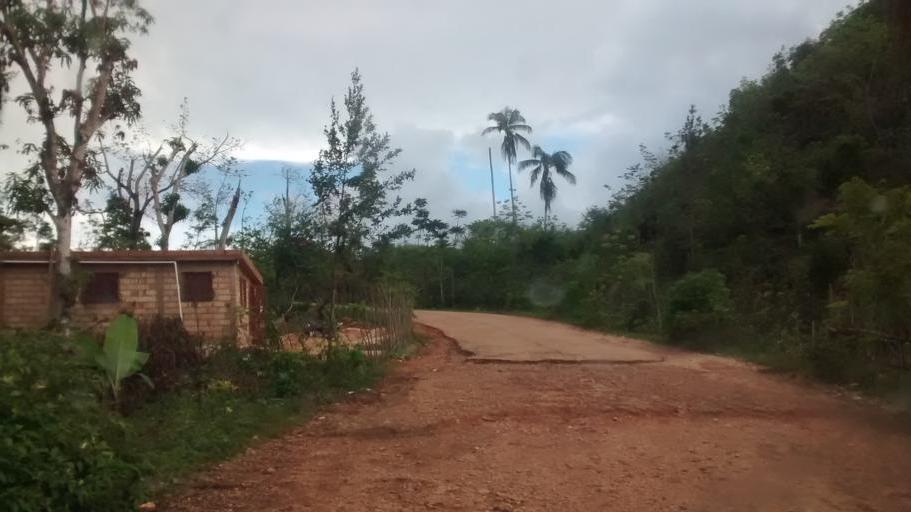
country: HT
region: Grandans
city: Corail
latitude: 18.5181
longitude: -73.7874
